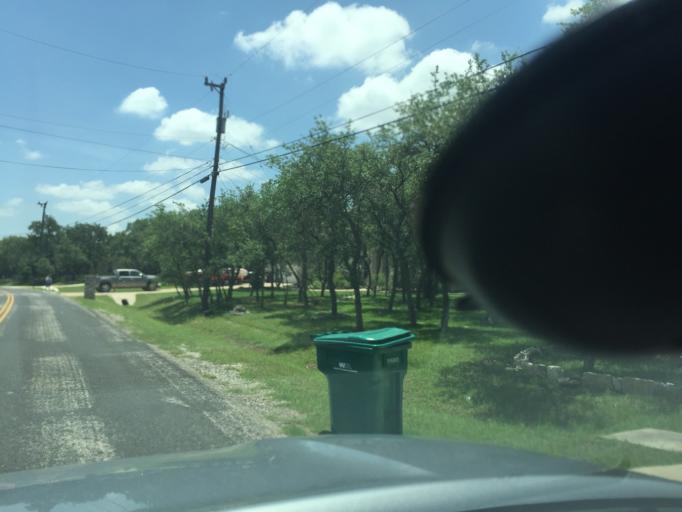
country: US
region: Texas
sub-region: Bexar County
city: Timberwood Park
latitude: 29.6989
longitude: -98.5066
